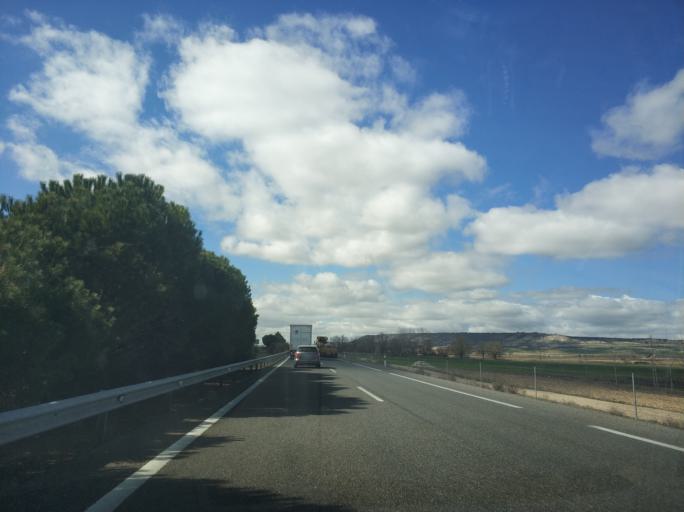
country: ES
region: Castille and Leon
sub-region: Provincia de Palencia
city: Villodrigo
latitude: 42.1368
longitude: -4.1133
